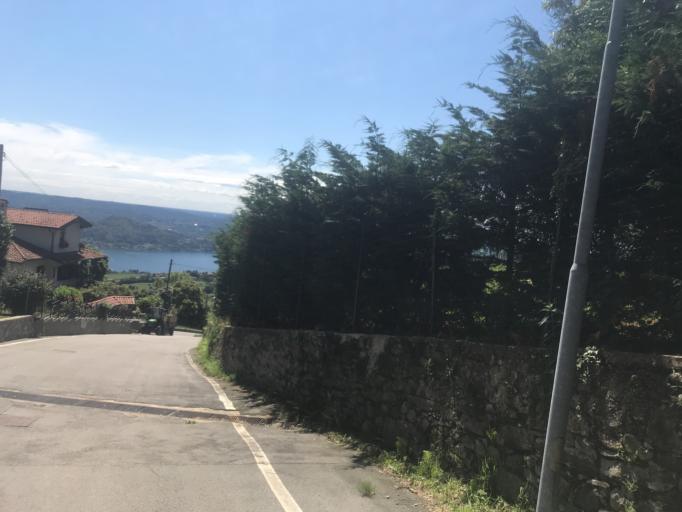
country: IT
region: Piedmont
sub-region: Provincia di Novara
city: Pisano
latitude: 45.8053
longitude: 8.5108
